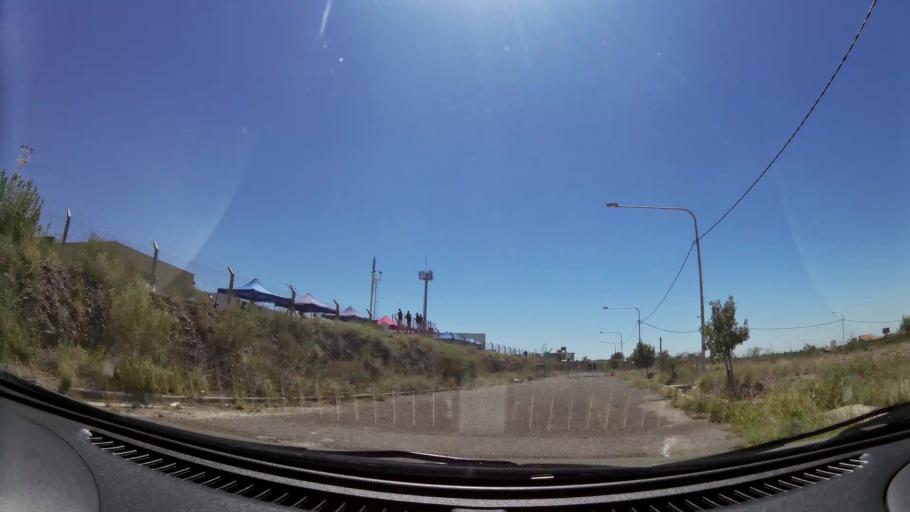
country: AR
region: Mendoza
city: Las Heras
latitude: -32.8513
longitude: -68.8574
